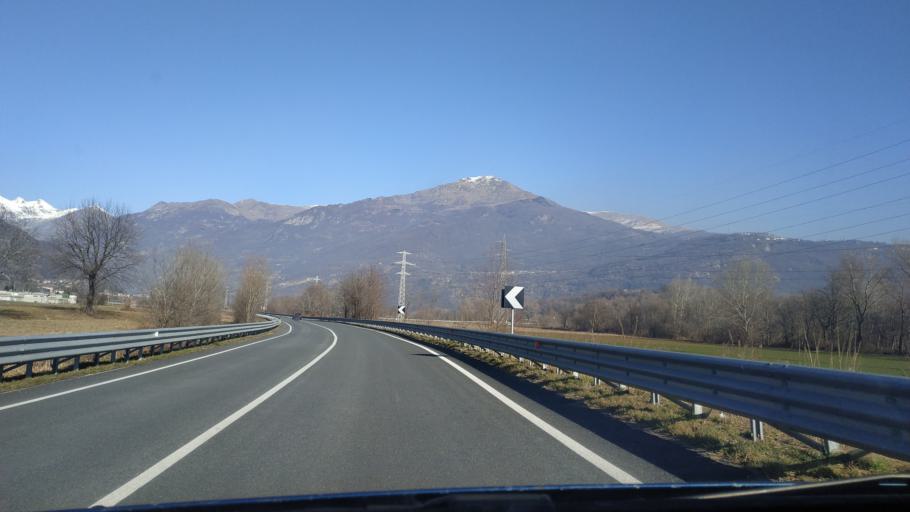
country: IT
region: Piedmont
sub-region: Provincia di Torino
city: Quassolo
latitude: 45.5038
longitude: 7.8351
